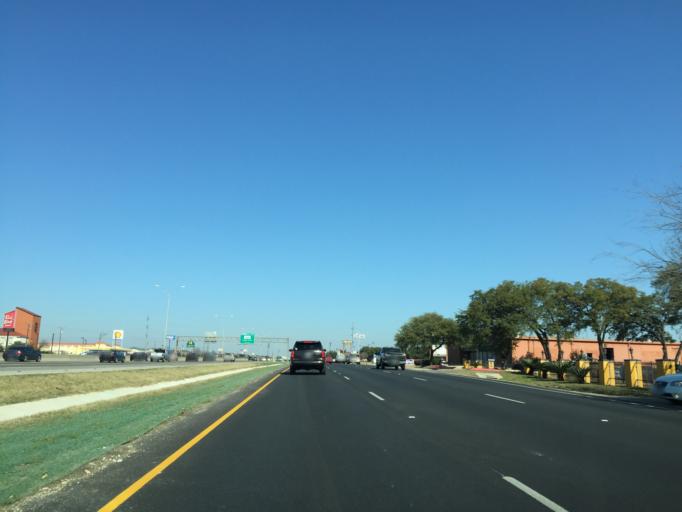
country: US
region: Texas
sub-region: Williamson County
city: Round Rock
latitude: 30.5262
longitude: -97.6899
